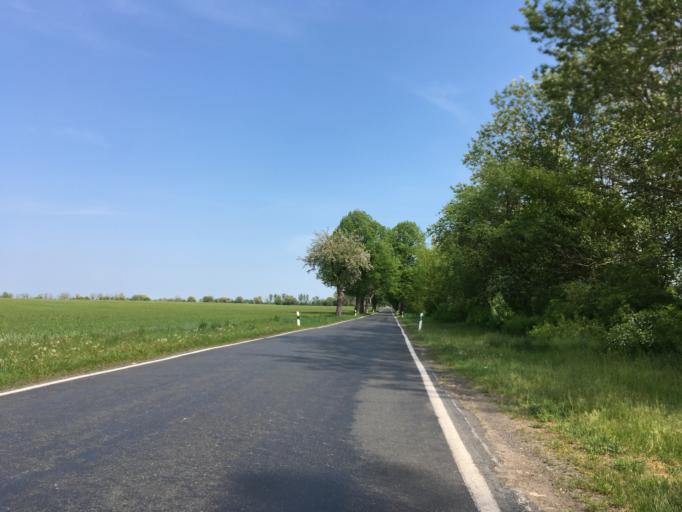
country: DE
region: Brandenburg
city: Werneuchen
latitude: 52.6718
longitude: 13.7343
